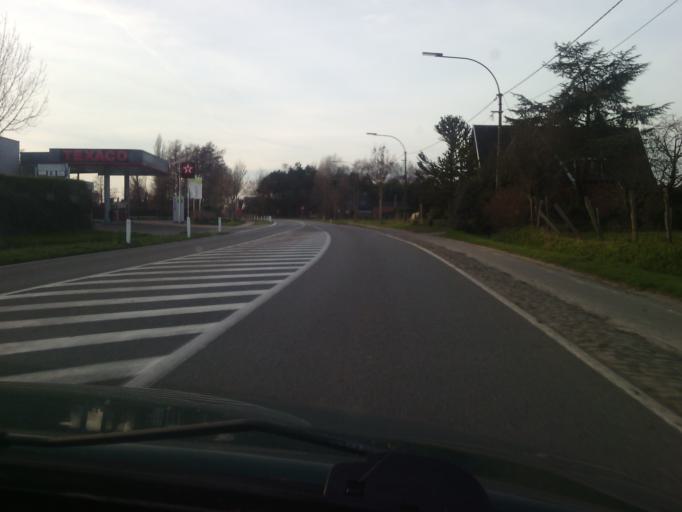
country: BE
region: Flanders
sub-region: Provincie Oost-Vlaanderen
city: Wichelen
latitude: 51.0465
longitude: 3.9337
